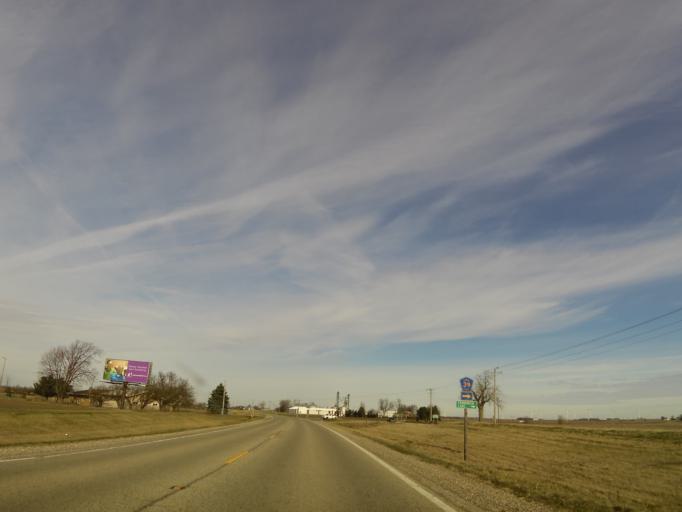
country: US
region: Illinois
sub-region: McLean County
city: Twin Grove
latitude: 40.5152
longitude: -89.0402
